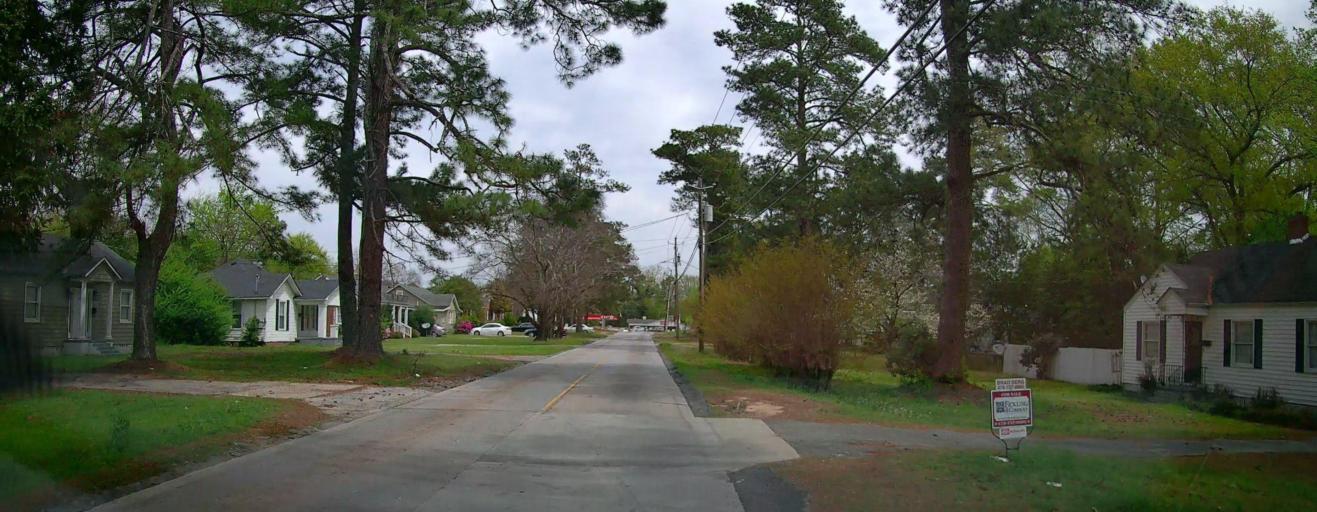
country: US
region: Georgia
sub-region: Bibb County
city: Macon
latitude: 32.8602
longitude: -83.6930
